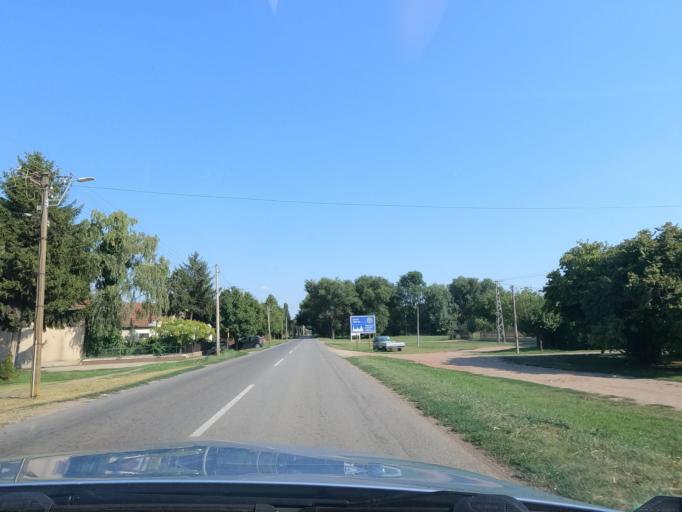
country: RS
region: Autonomna Pokrajina Vojvodina
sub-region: Juznobacki Okrug
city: Becej
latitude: 45.6307
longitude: 20.0173
